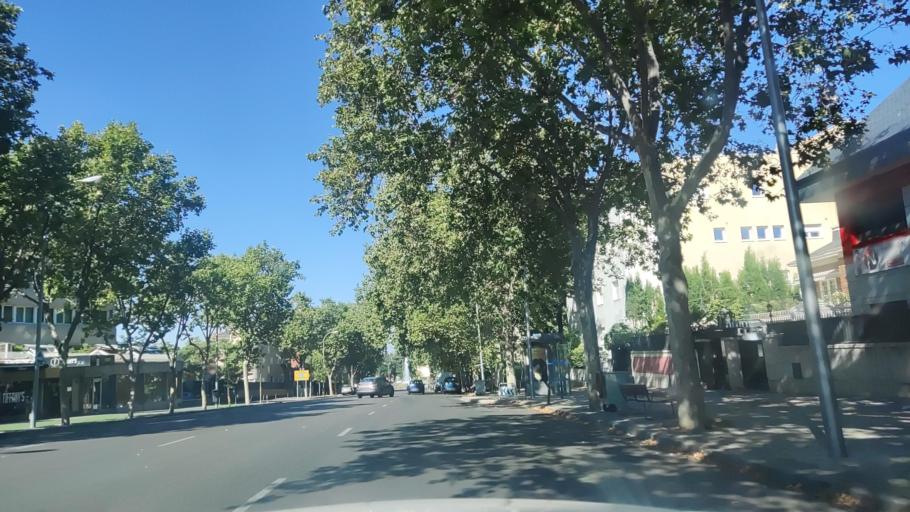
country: ES
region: Madrid
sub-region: Provincia de Madrid
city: Salamanca
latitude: 40.4460
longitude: -3.6829
